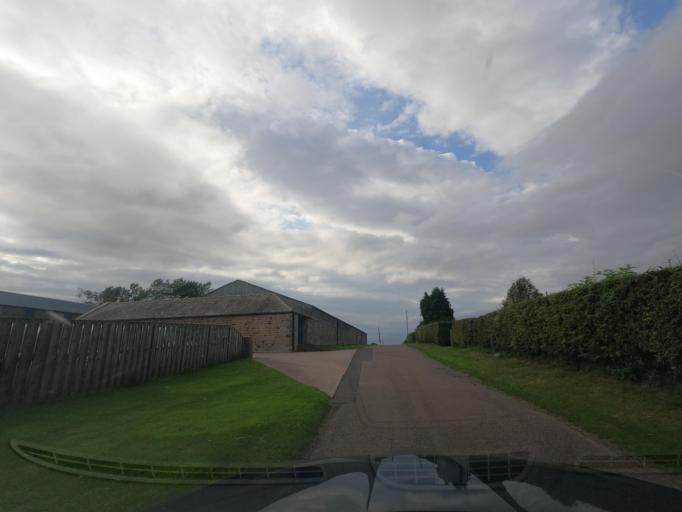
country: GB
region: England
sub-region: Northumberland
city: Ancroft
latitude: 55.7203
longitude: -2.0604
